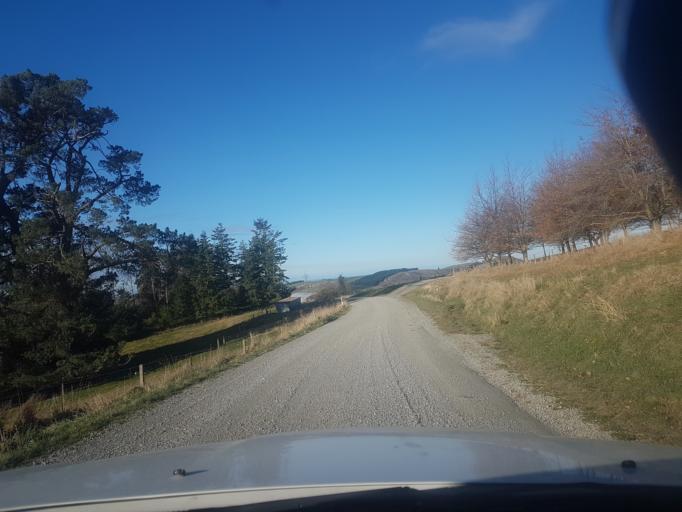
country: NZ
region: Canterbury
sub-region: Timaru District
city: Pleasant Point
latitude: -44.1689
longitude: 170.9212
